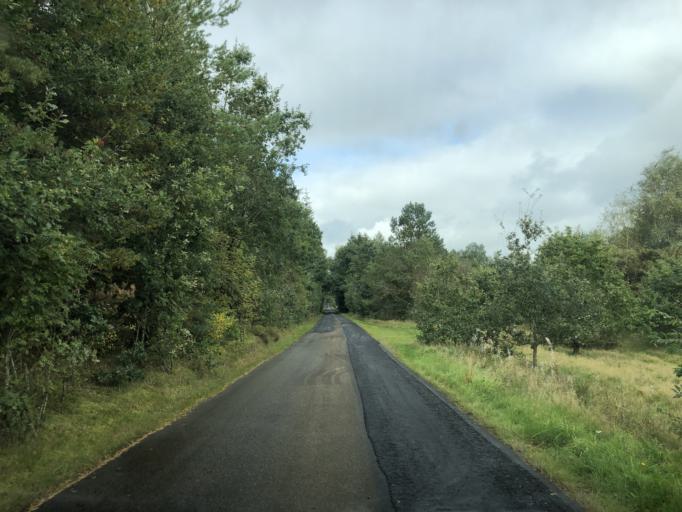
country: DK
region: Central Jutland
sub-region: Holstebro Kommune
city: Ulfborg
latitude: 56.3038
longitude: 8.4360
